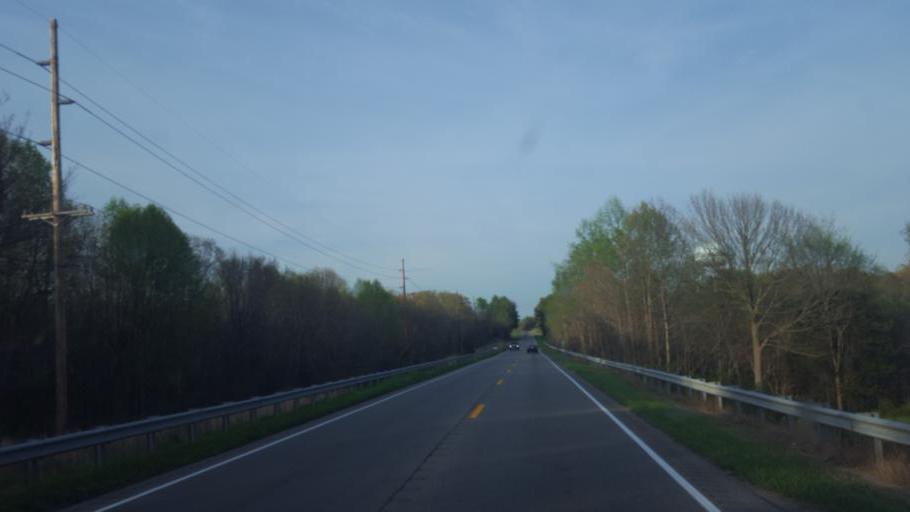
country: US
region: Kentucky
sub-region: Barren County
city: Glasgow
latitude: 36.9610
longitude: -85.9529
